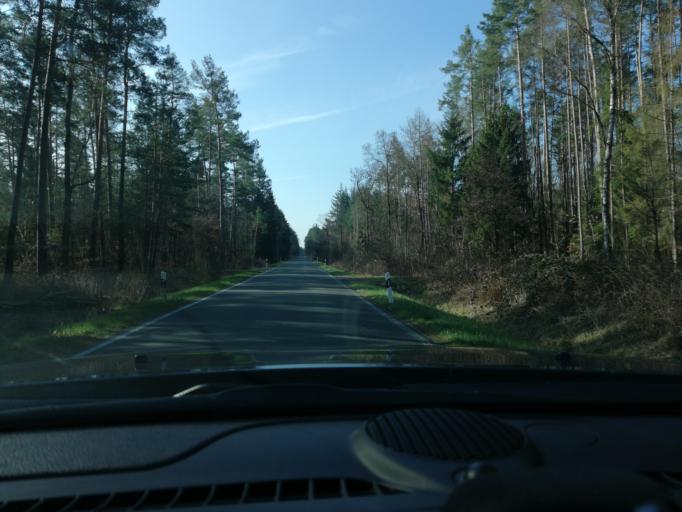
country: DE
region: Bavaria
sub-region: Regierungsbezirk Mittelfranken
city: Hessdorf
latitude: 49.6180
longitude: 10.9384
